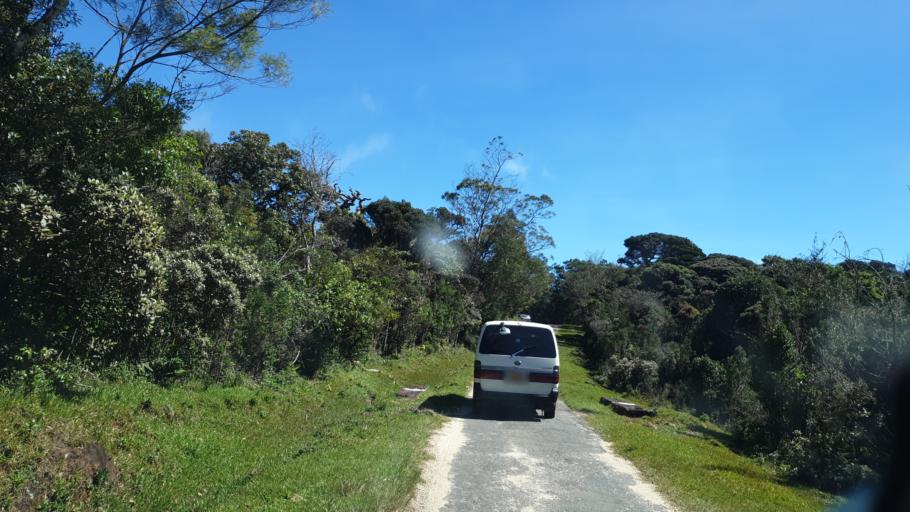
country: LK
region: Uva
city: Haputale
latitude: 6.7993
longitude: 80.8330
